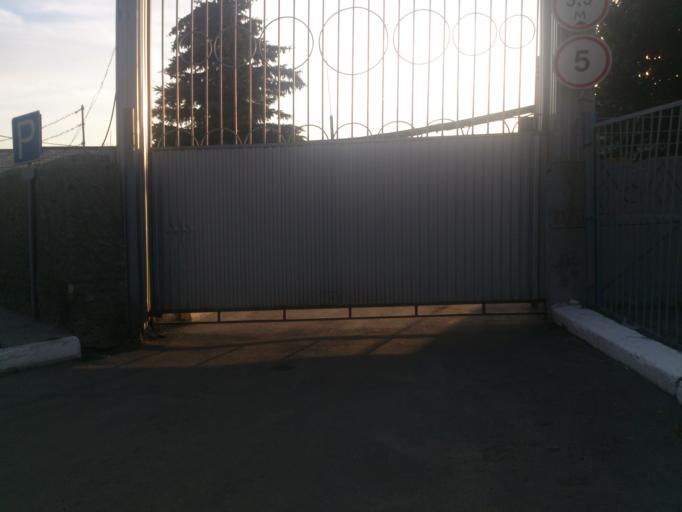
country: RU
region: Ulyanovsk
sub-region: Ulyanovskiy Rayon
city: Ulyanovsk
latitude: 54.2916
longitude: 48.3670
